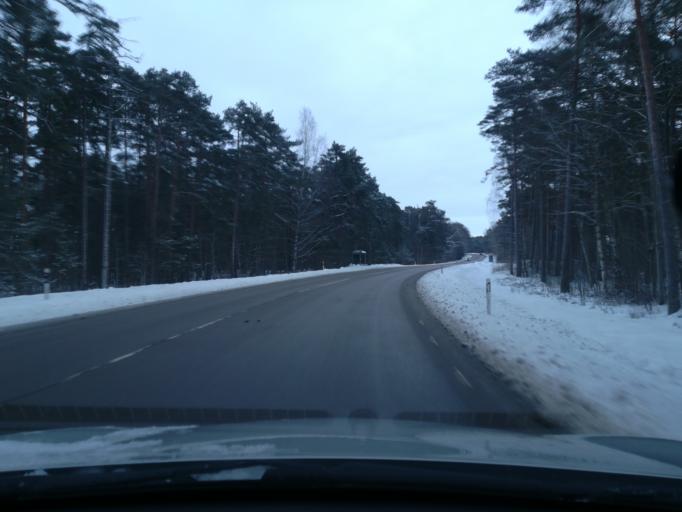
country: EE
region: Harju
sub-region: Keila linn
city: Keila
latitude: 59.4103
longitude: 24.2995
